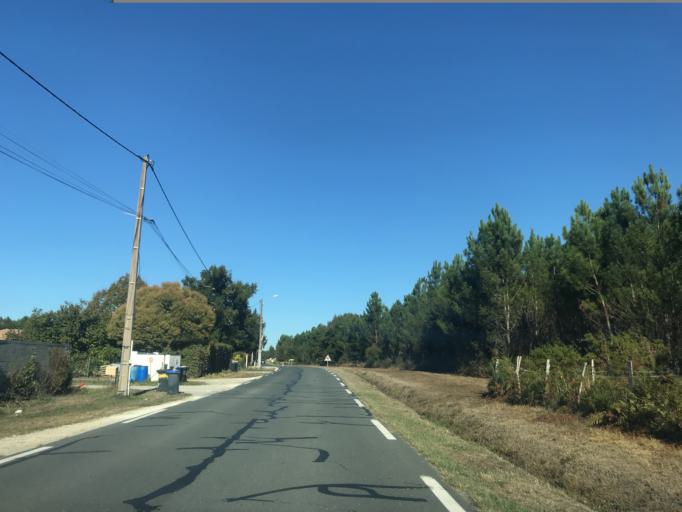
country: FR
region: Aquitaine
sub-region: Departement de la Gironde
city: Mios
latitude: 44.6364
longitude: -0.8893
